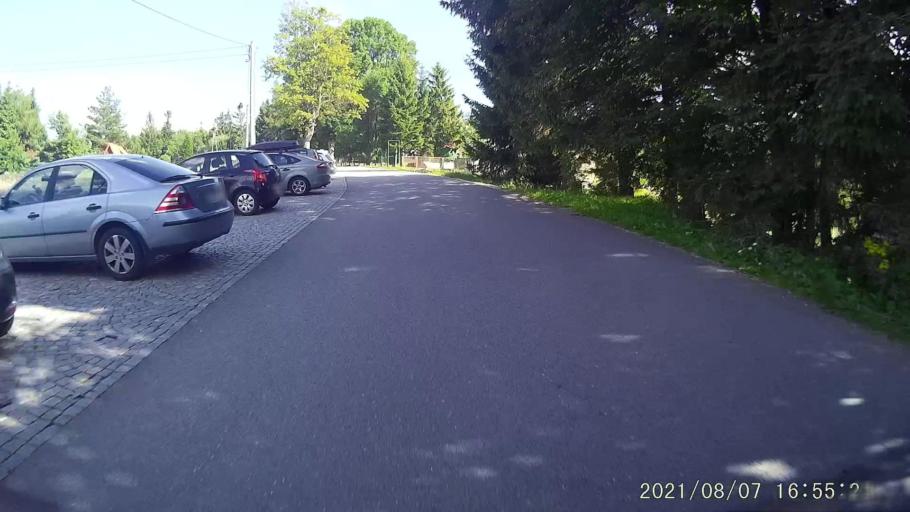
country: PL
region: Lower Silesian Voivodeship
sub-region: Powiat klodzki
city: Bystrzyca Klodzka
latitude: 50.2779
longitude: 16.5368
